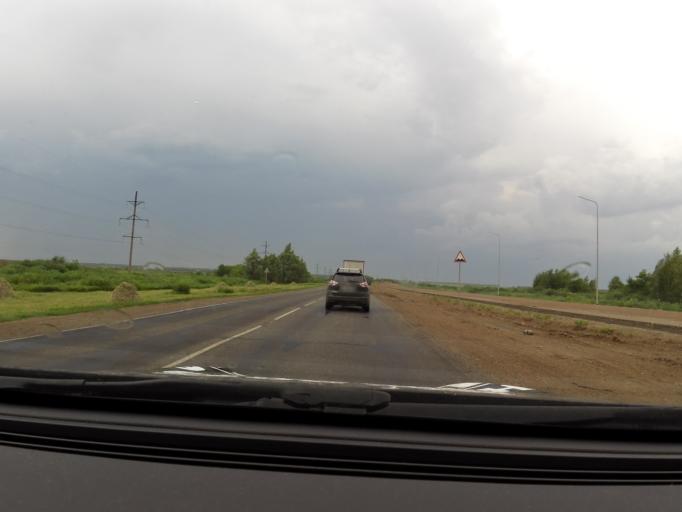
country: RU
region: Bashkortostan
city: Asanovo
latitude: 54.9052
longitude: 55.6165
